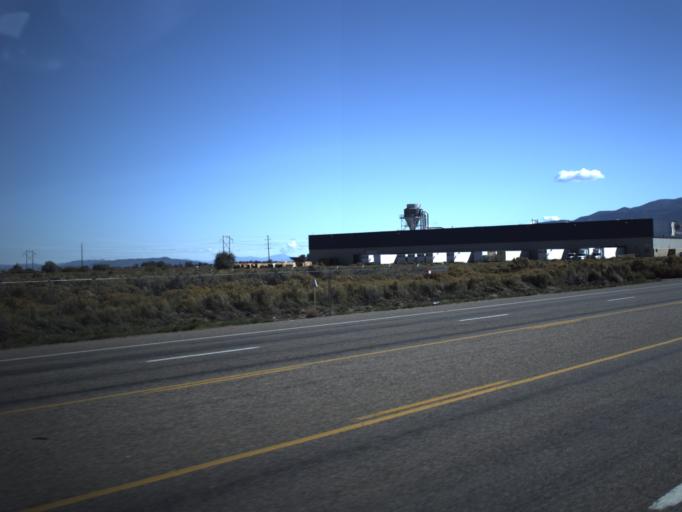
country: US
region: Utah
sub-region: Iron County
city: Cedar City
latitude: 37.6849
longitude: -113.1532
